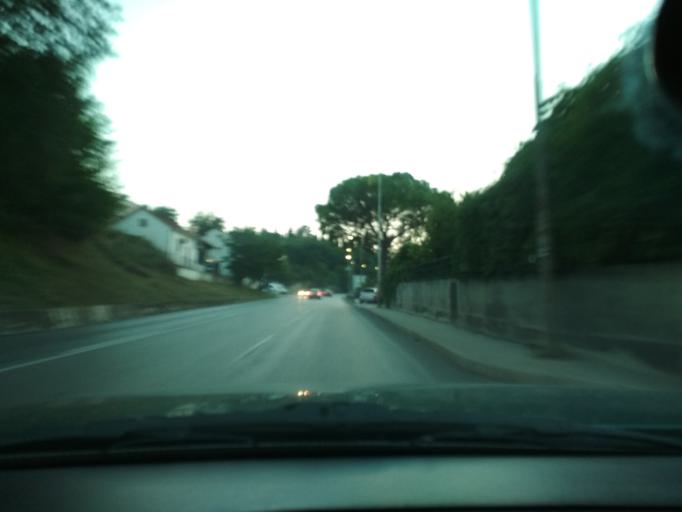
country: ME
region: Herceg Novi
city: Herceg-Novi
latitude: 42.4547
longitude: 18.5471
